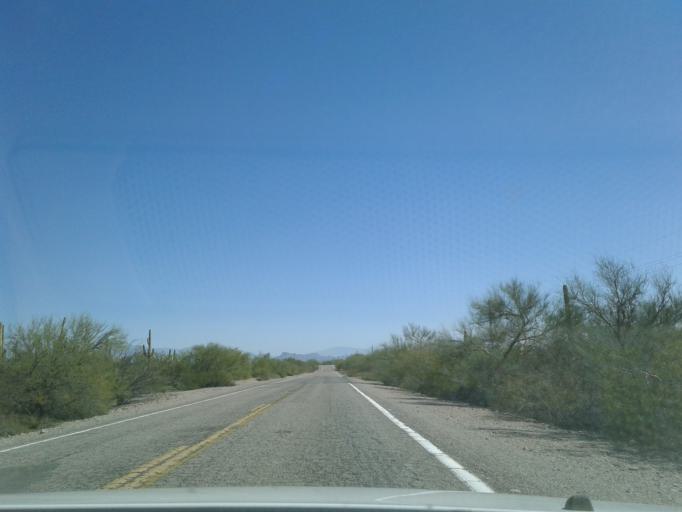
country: US
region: Arizona
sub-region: Pima County
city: Avra Valley
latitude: 32.3742
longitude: -111.4588
